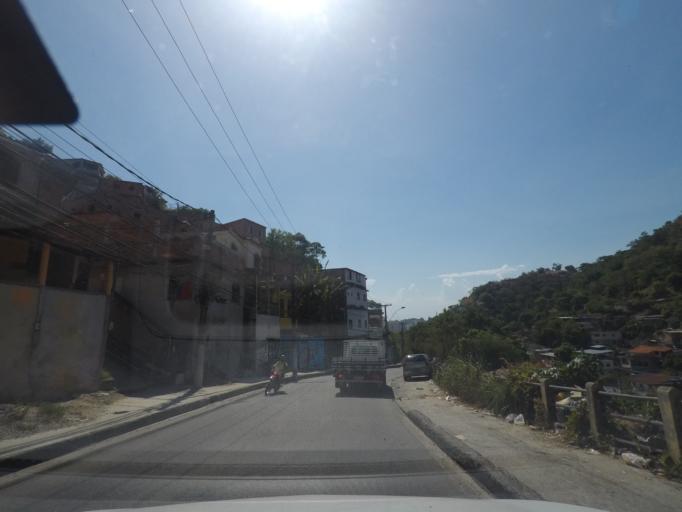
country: BR
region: Rio de Janeiro
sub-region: Niteroi
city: Niteroi
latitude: -22.9066
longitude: -43.0800
